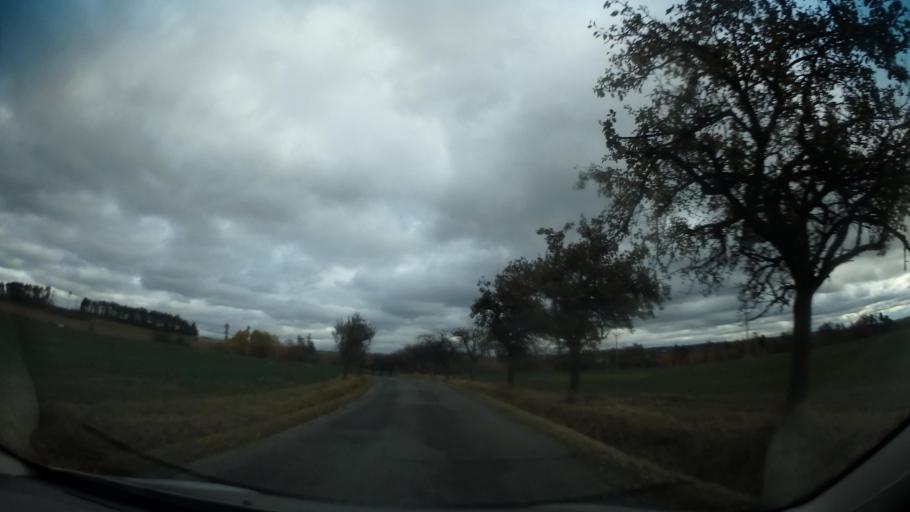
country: CZ
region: Vysocina
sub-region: Okres Zd'ar nad Sazavou
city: Velka Bites
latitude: 49.2900
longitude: 16.1532
